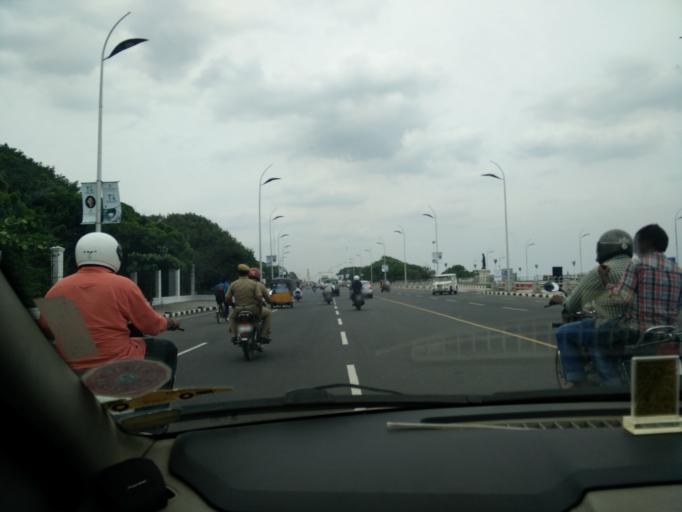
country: IN
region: Tamil Nadu
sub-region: Chennai
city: Gandhi Nagar
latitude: 13.0403
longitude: 80.2791
